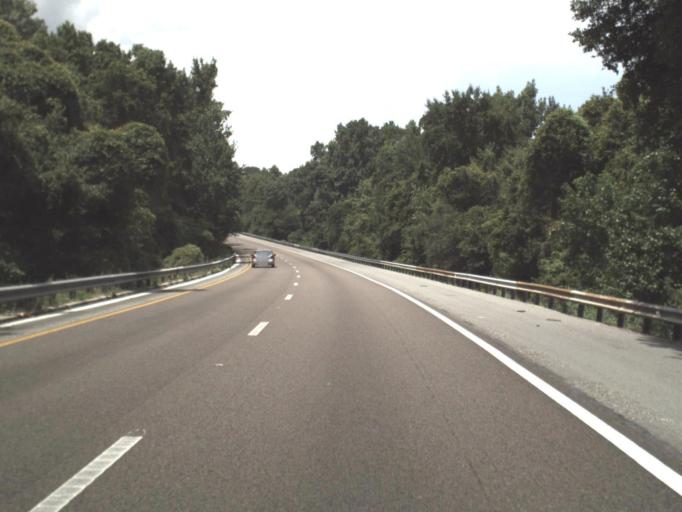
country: US
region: Florida
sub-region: Hernando County
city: Hill 'n Dale
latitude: 28.4663
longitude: -82.2732
